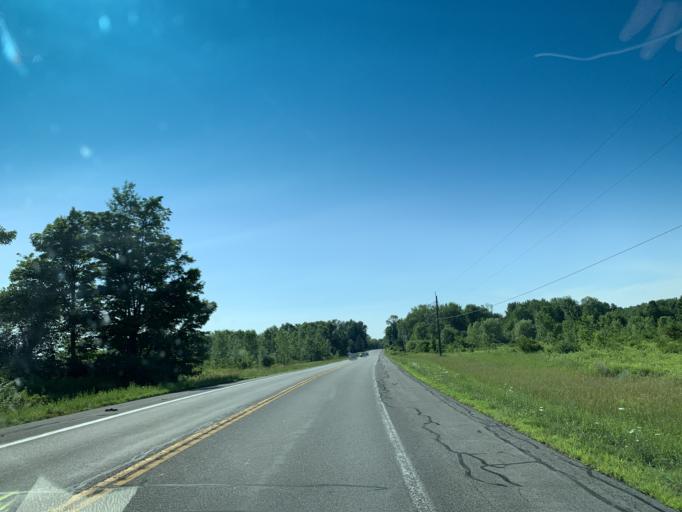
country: US
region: New York
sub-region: Madison County
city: Oneida
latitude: 43.1346
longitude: -75.6066
